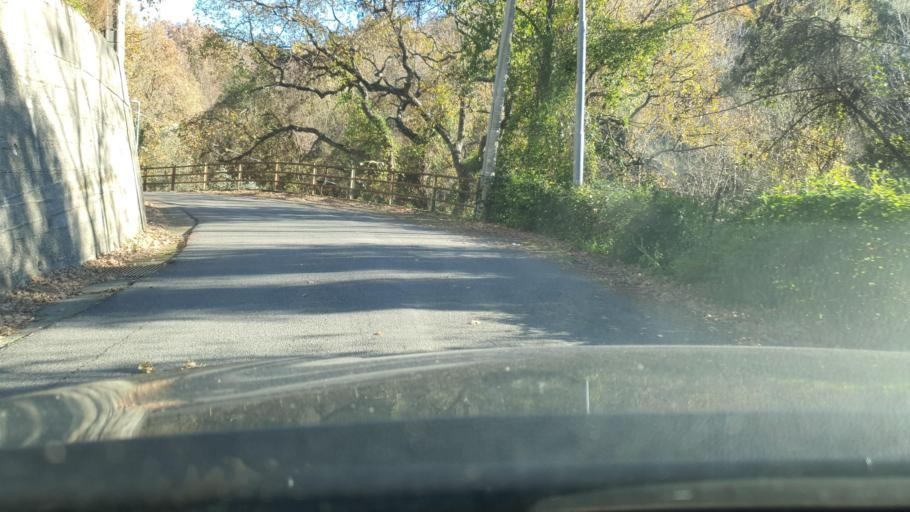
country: IT
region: Calabria
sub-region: Provincia di Catanzaro
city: Sant'Elia
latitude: 38.9614
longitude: 16.5797
